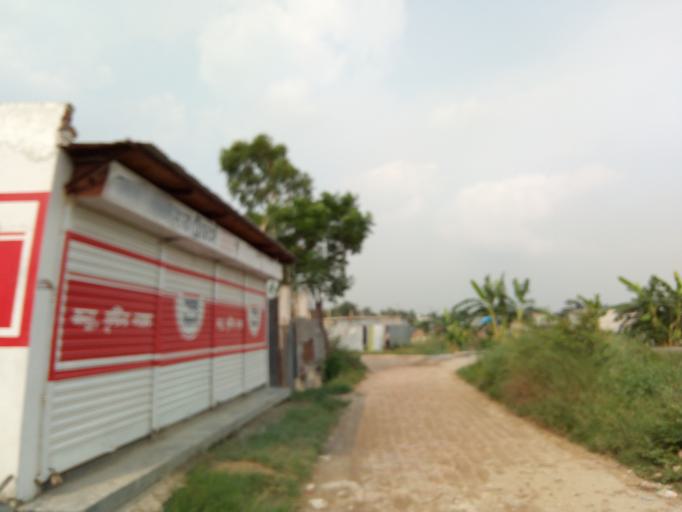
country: BD
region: Dhaka
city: Paltan
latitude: 23.7604
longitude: 90.4663
